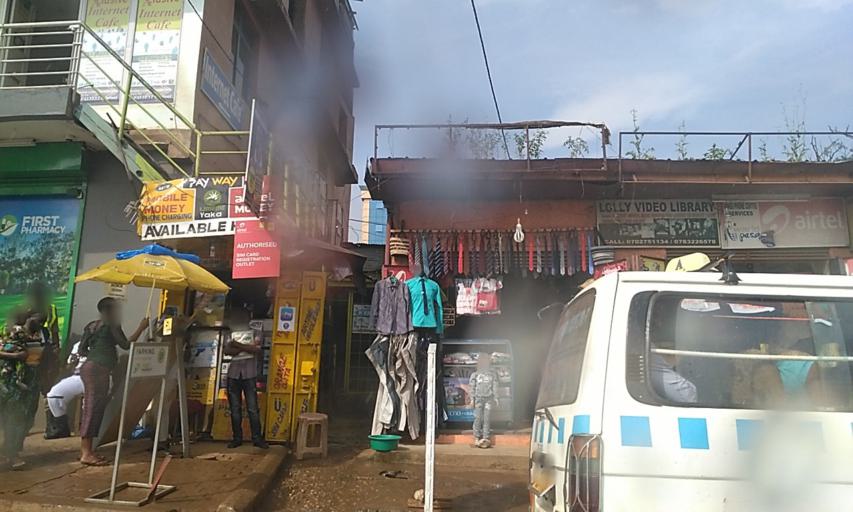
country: UG
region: Central Region
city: Kampala Central Division
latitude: 0.3319
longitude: 32.5738
